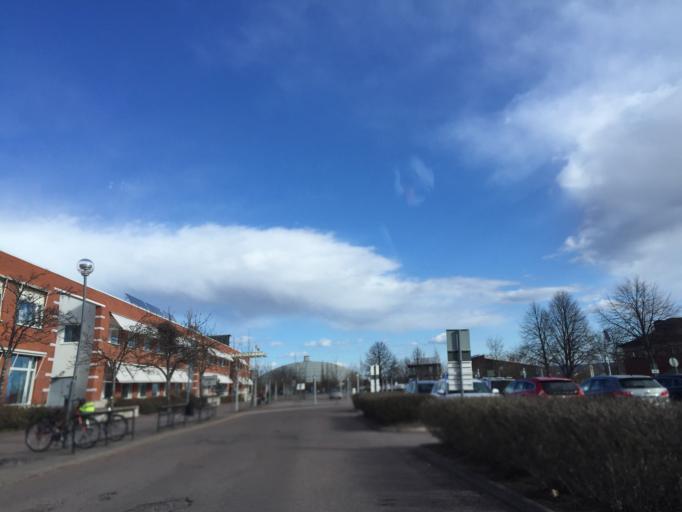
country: SE
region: Dalarna
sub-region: Borlange Kommun
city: Borlaenge
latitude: 60.4873
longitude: 15.4080
